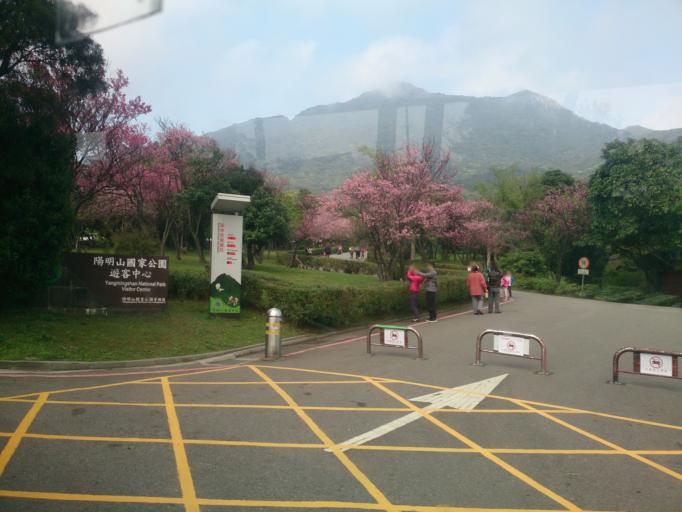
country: TW
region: Taipei
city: Taipei
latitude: 25.1553
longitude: 121.5462
